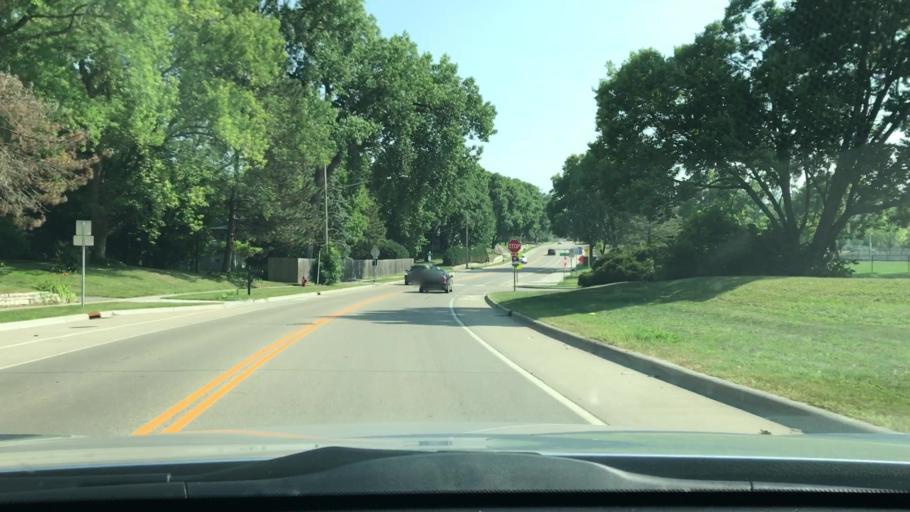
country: US
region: Minnesota
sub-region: Hennepin County
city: Edina
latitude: 44.8921
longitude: -93.3691
